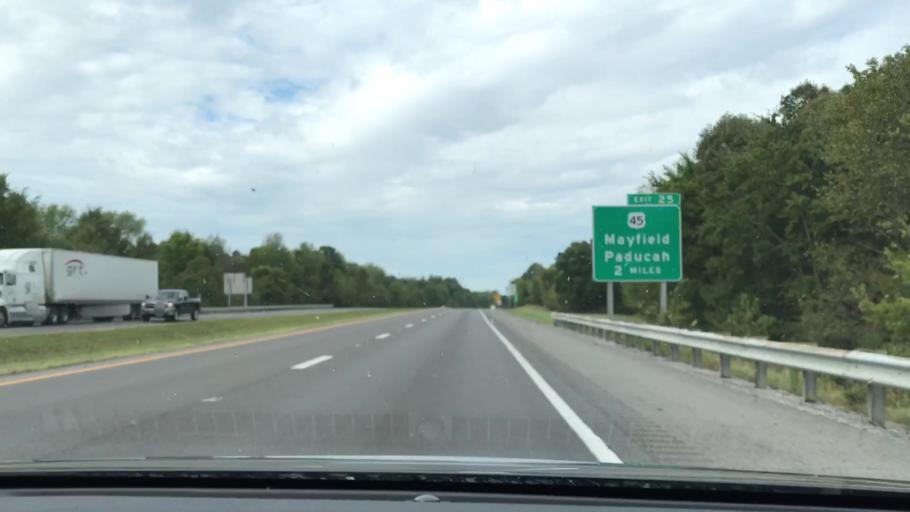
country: US
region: Kentucky
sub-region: Graves County
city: Mayfield
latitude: 36.7732
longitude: -88.6026
